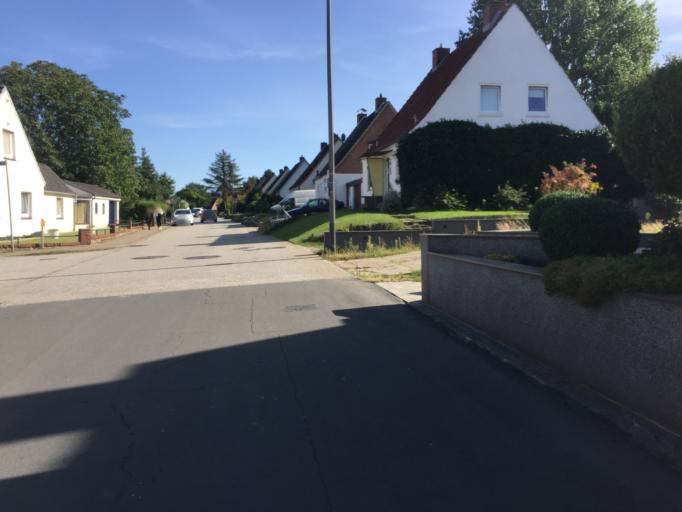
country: DE
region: Schleswig-Holstein
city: Itzehoe
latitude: 53.9083
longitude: 9.4938
